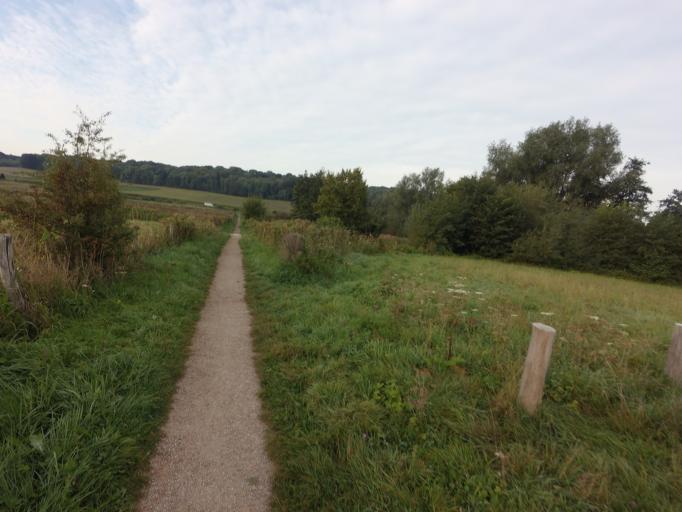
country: NL
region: Limburg
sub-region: Valkenburg aan de Geul
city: Valkenburg
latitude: 50.8573
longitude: 5.8446
